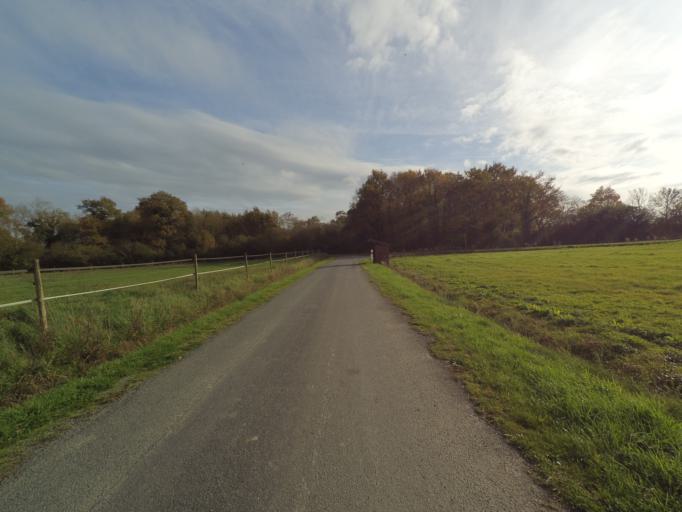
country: FR
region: Pays de la Loire
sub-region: Departement de la Vendee
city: Saint-Hilaire-de-Loulay
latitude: 47.0370
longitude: -1.3347
